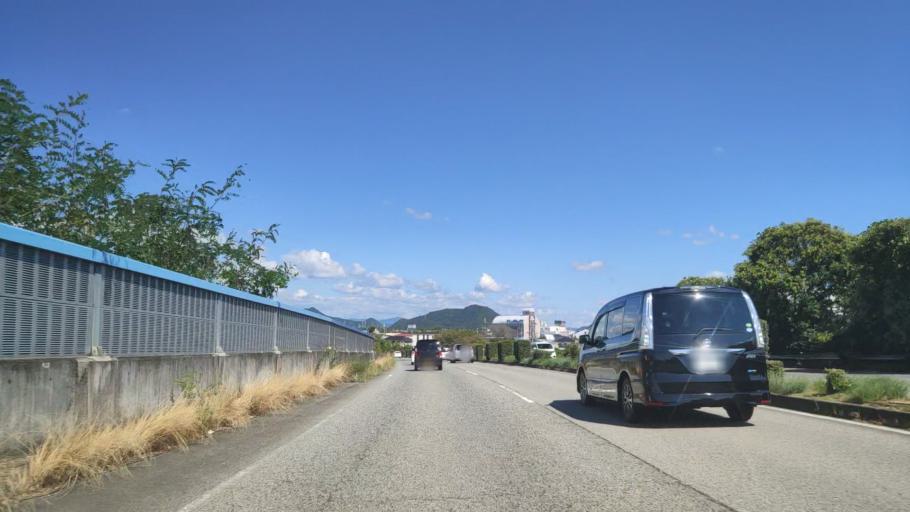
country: JP
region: Hyogo
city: Yashiro
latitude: 34.9241
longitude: 134.9600
